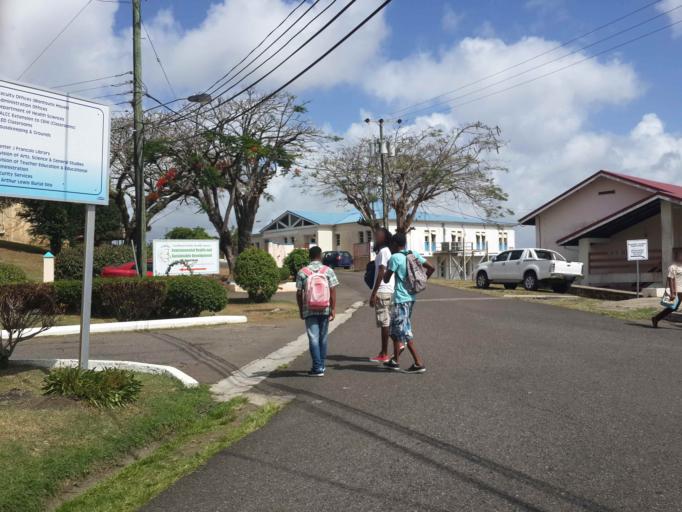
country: LC
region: Castries Quarter
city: Castries
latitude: 13.9977
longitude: -60.9951
